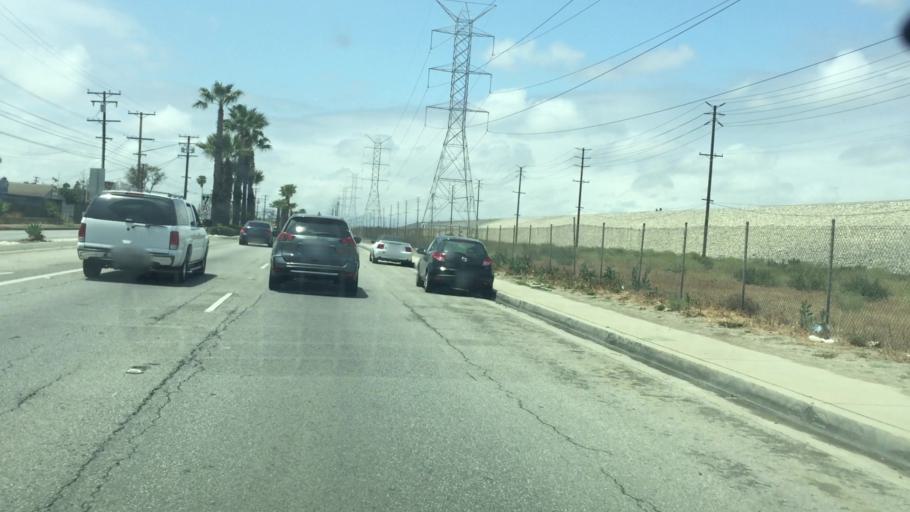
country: US
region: California
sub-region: Los Angeles County
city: Irwindale
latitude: 34.1071
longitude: -117.9443
